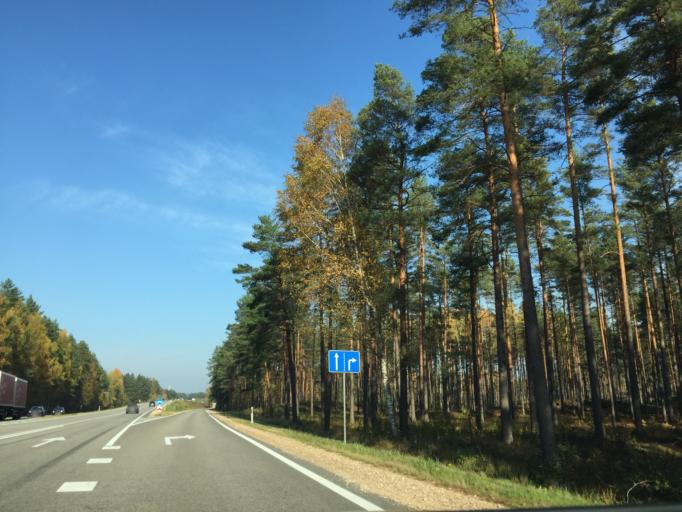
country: LV
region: Babite
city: Pinki
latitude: 56.9170
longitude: 23.9142
